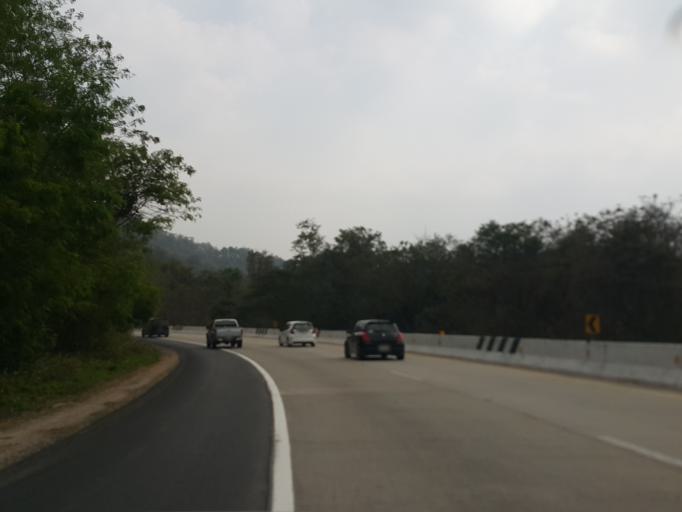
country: TH
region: Lamphun
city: Mae Tha
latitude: 18.3769
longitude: 99.2287
